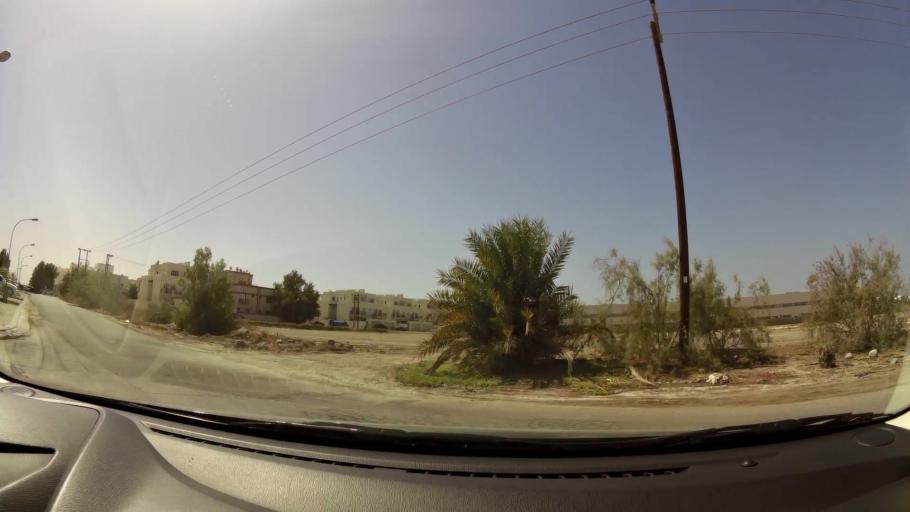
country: OM
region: Muhafazat Masqat
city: Bawshar
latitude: 23.5985
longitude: 58.3495
